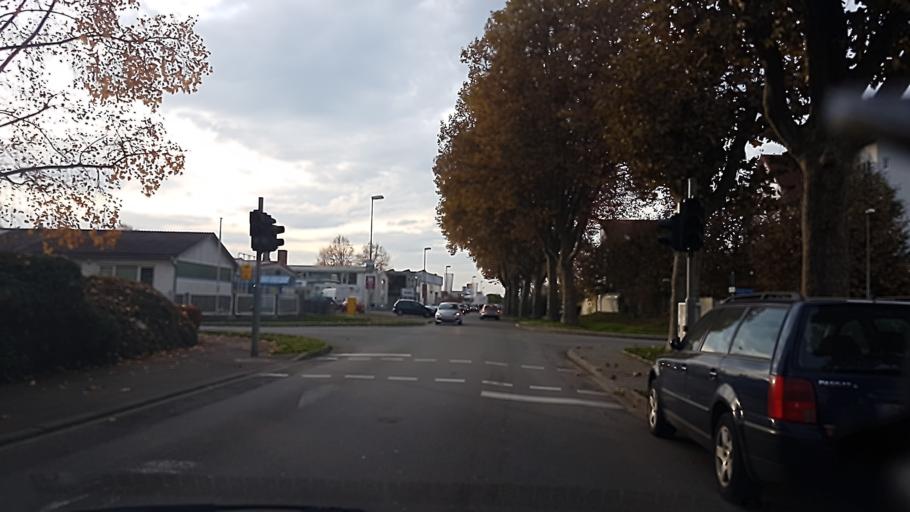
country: DE
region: Baden-Wuerttemberg
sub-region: Freiburg Region
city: Endingen
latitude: 48.1474
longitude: 7.7038
